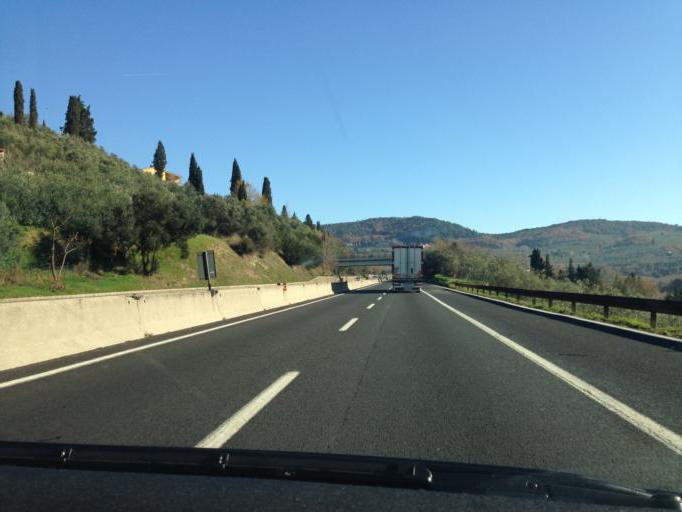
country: IT
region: Tuscany
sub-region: Province of Florence
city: Antella
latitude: 43.7295
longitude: 11.3592
